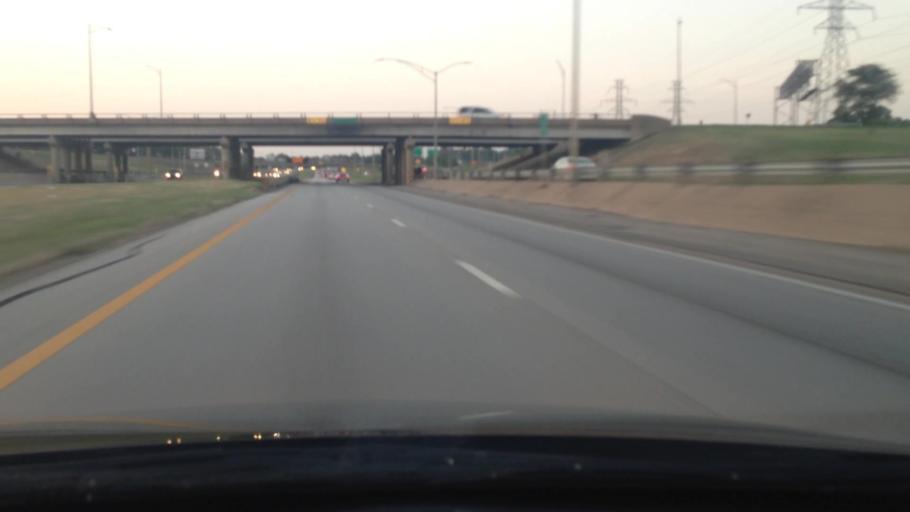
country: US
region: Texas
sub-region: Tarrant County
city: Pantego
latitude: 32.7337
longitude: -97.2251
